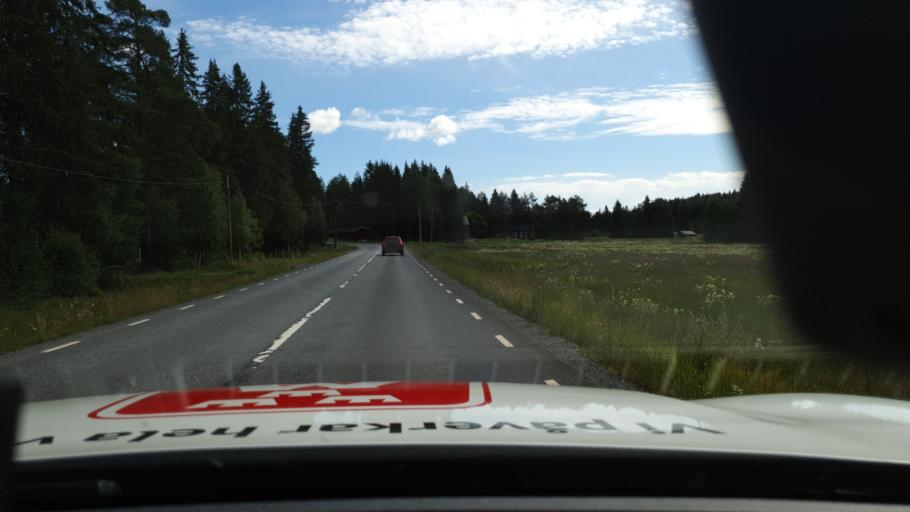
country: SE
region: Norrbotten
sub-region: Lulea Kommun
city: Ranea
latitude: 65.7839
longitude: 22.1640
